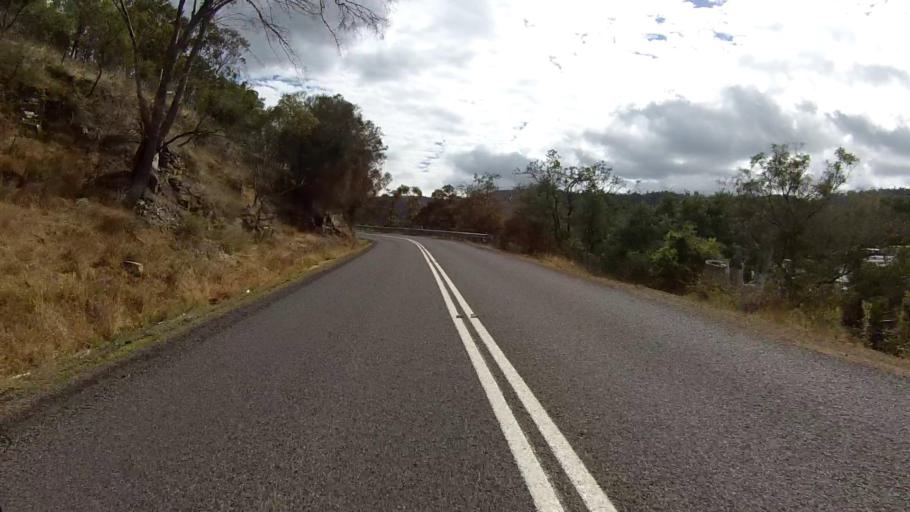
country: AU
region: Tasmania
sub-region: Clarence
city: Lindisfarne
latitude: -42.8069
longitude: 147.3538
